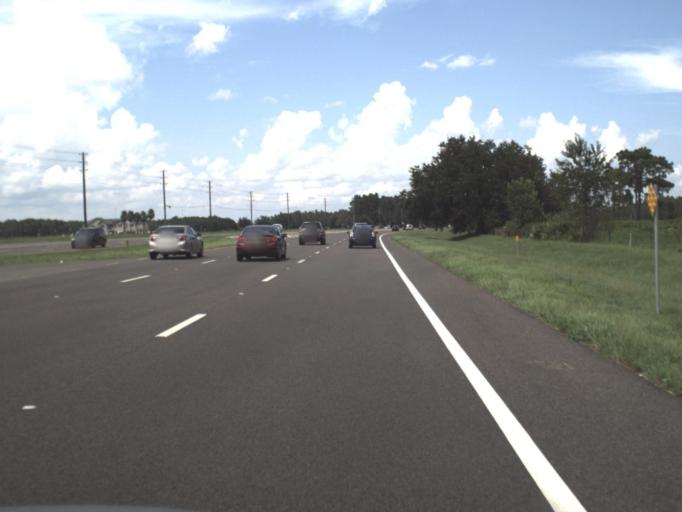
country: US
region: Florida
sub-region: Pasco County
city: Wesley Chapel
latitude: 28.2211
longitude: -82.3532
